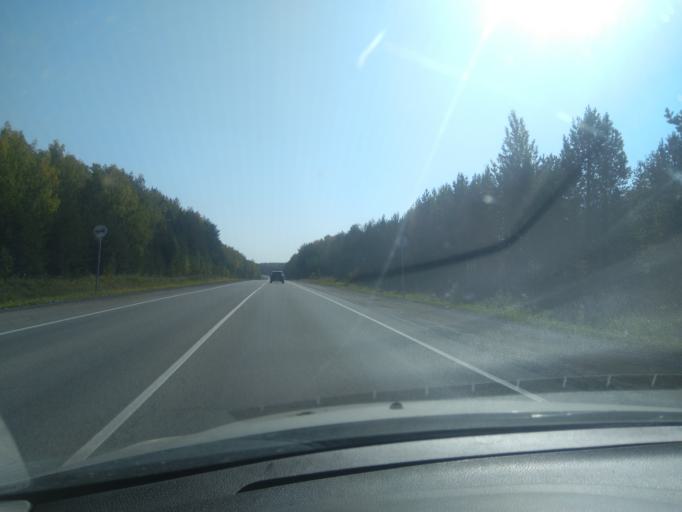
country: RU
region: Sverdlovsk
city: Verkhneye Dubrovo
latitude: 56.7146
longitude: 61.0587
